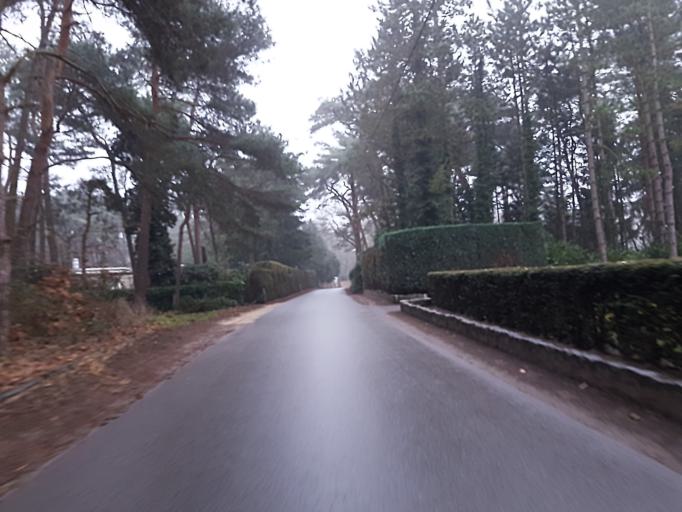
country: BE
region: Flanders
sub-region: Provincie Vlaams-Brabant
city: Keerbergen
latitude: 51.0024
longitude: 4.6016
